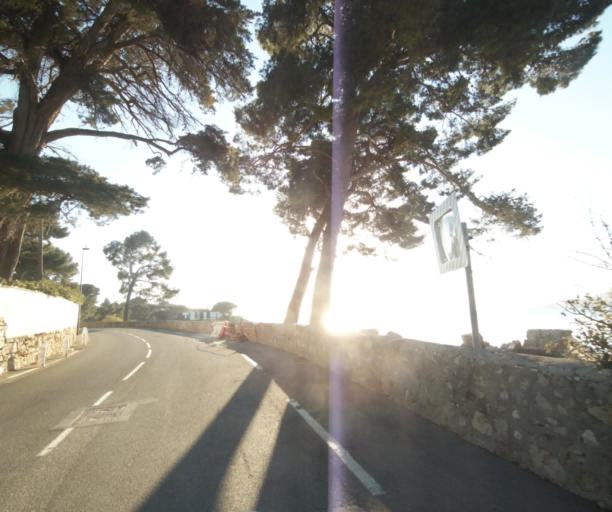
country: FR
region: Provence-Alpes-Cote d'Azur
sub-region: Departement des Alpes-Maritimes
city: Antibes
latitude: 43.5538
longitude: 7.1224
